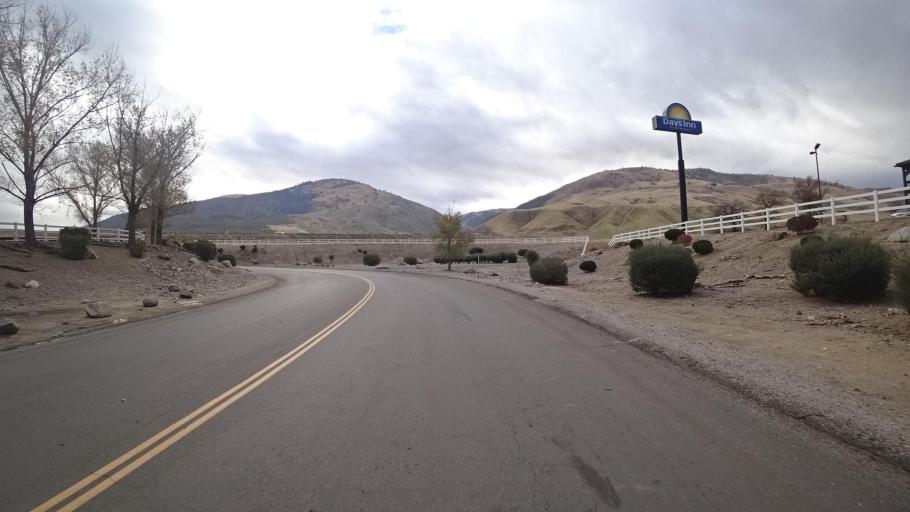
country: US
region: California
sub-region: Kern County
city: Frazier Park
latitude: 34.9394
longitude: -118.9322
